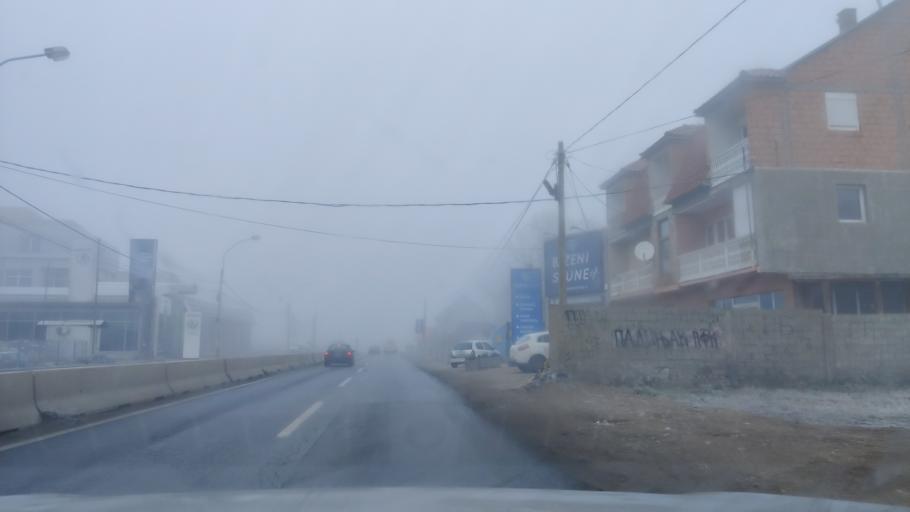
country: RS
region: Central Serbia
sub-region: Belgrade
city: Stari Grad
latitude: 44.8594
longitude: 20.4797
